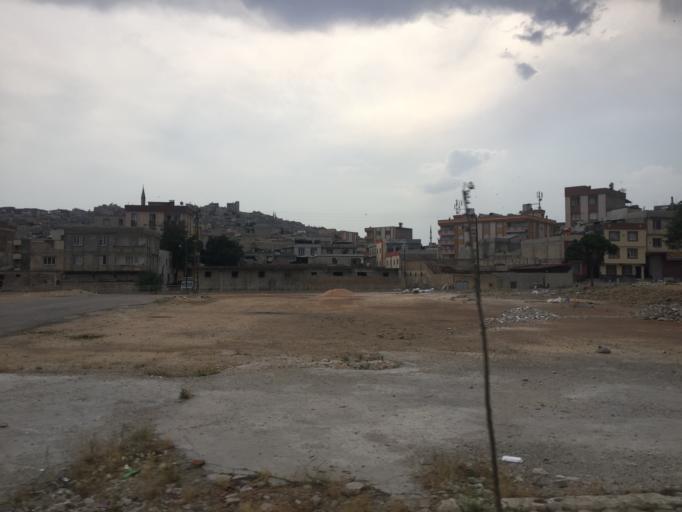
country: TR
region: Gaziantep
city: Gaziantep
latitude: 37.0727
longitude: 37.4130
